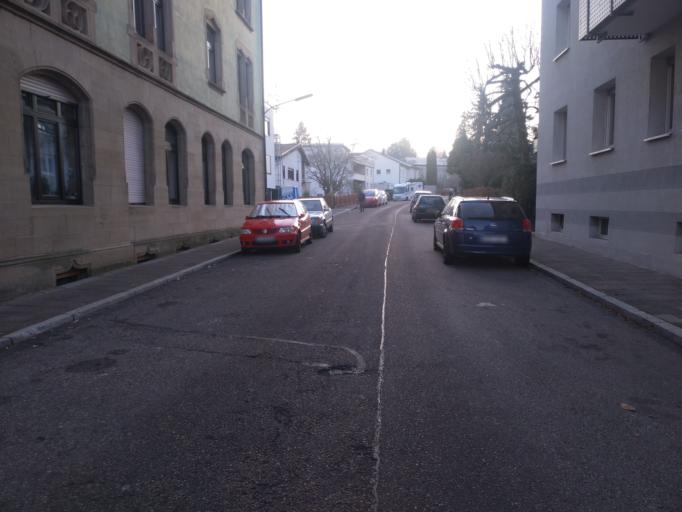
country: DE
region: Baden-Wuerttemberg
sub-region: Karlsruhe Region
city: Pforzheim
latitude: 48.8856
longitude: 8.6903
